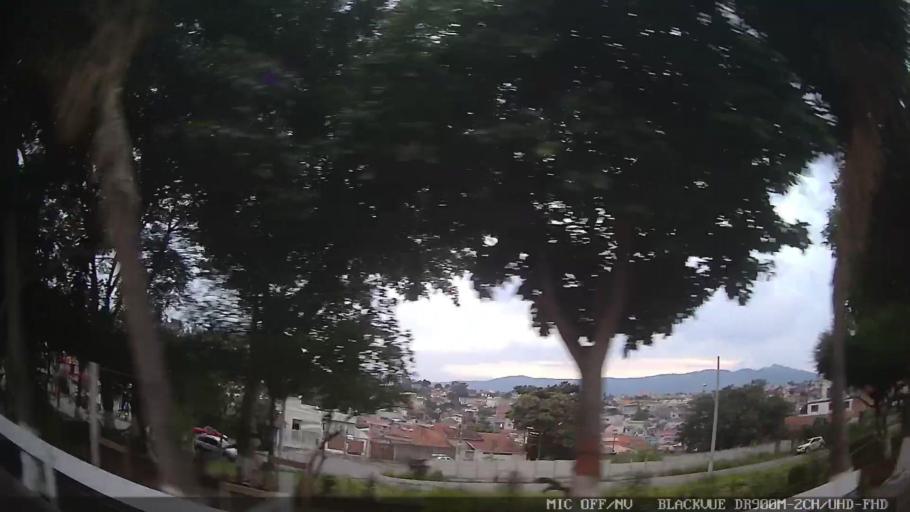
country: BR
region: Sao Paulo
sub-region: Atibaia
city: Atibaia
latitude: -23.1245
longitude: -46.5721
